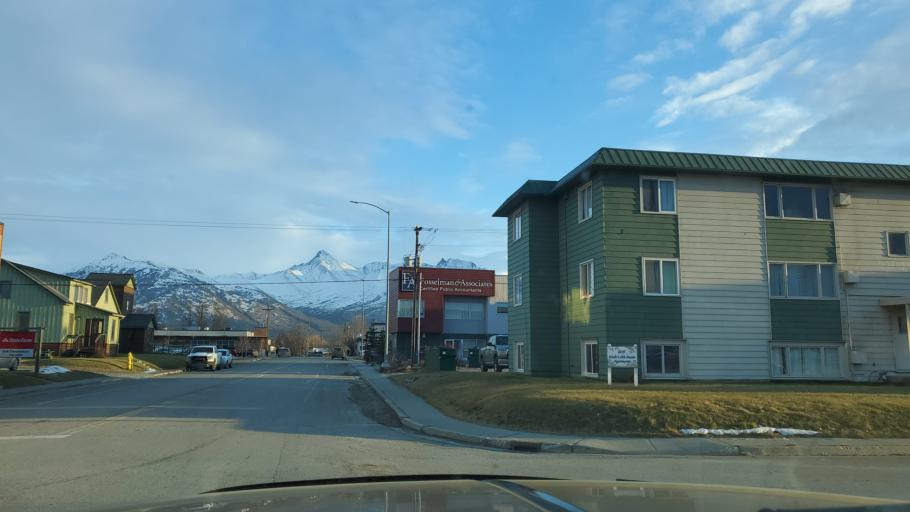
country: US
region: Alaska
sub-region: Matanuska-Susitna Borough
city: Palmer
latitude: 61.6013
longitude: -149.1185
